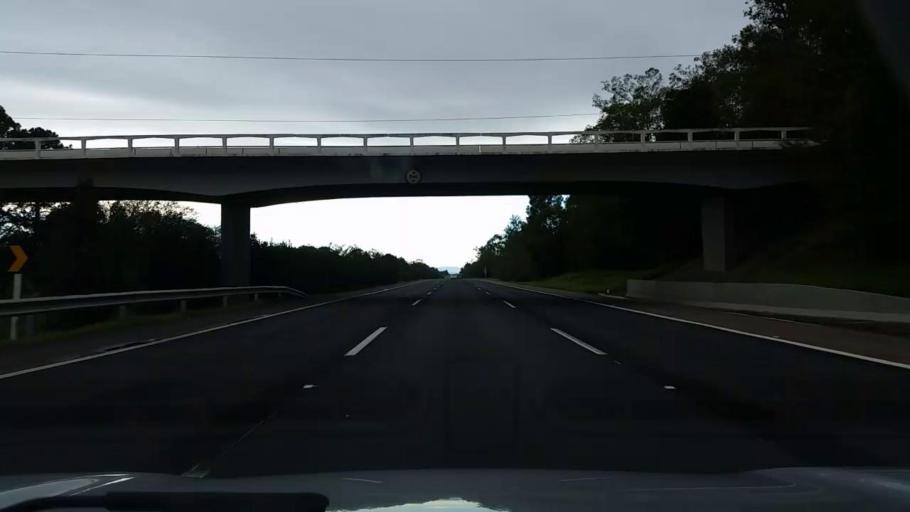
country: BR
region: Rio Grande do Sul
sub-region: Taquara
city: Taquara
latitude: -29.8903
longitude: -50.7047
